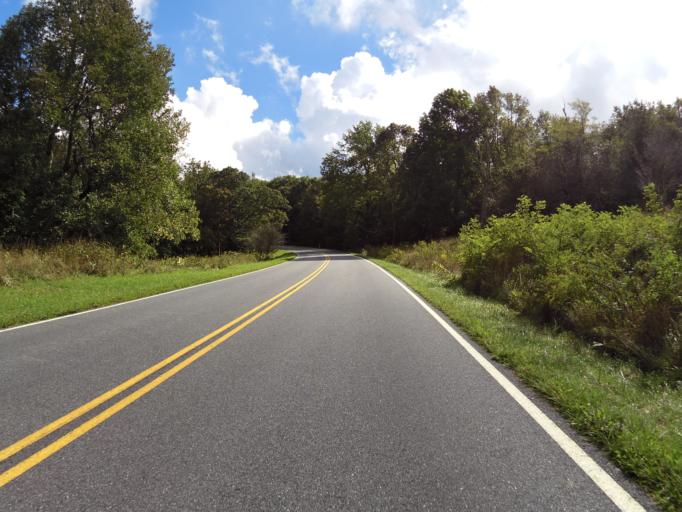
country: US
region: Virginia
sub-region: Page County
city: Stanley
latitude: 38.5730
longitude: -78.3836
